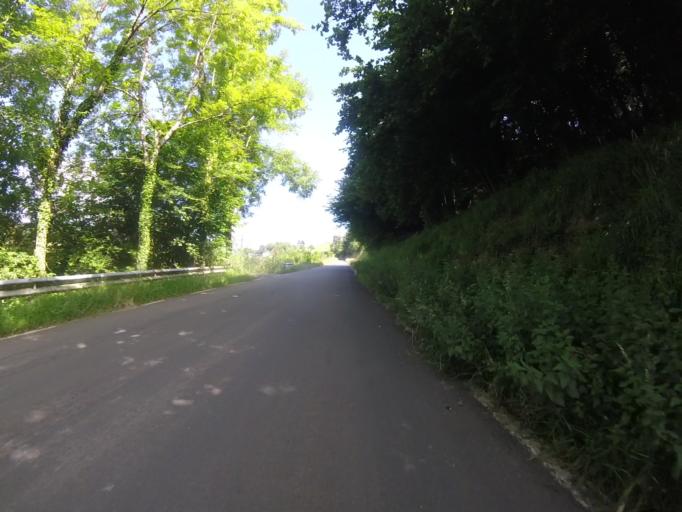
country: ES
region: Basque Country
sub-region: Provincia de Guipuzcoa
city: Ormaiztegui
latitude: 43.0848
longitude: -2.2414
